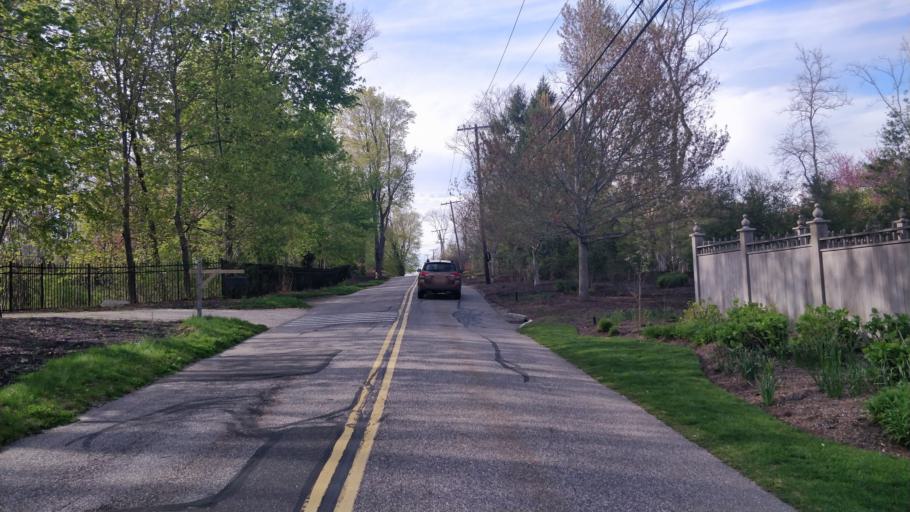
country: US
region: New York
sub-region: Suffolk County
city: East Setauket
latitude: 40.9728
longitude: -73.1181
